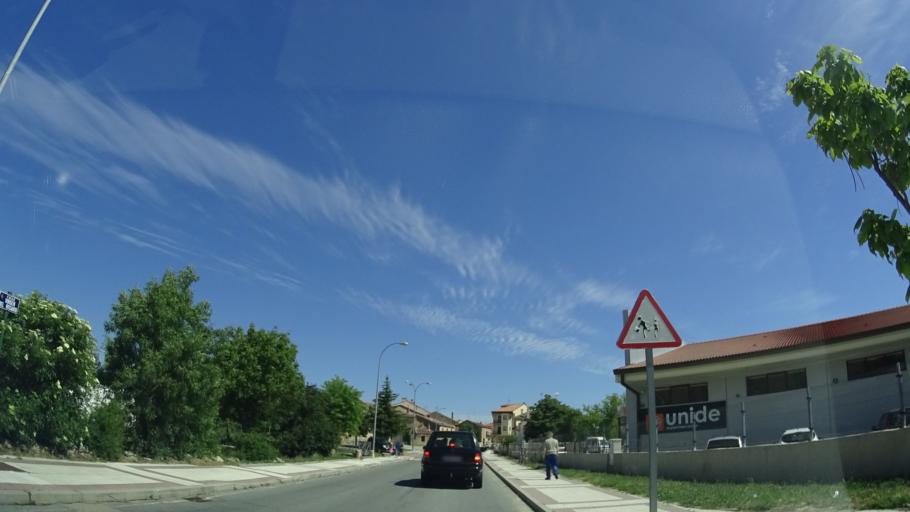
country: ES
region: Castille and Leon
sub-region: Provincia de Segovia
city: Pradena
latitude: 41.1356
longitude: -3.6884
